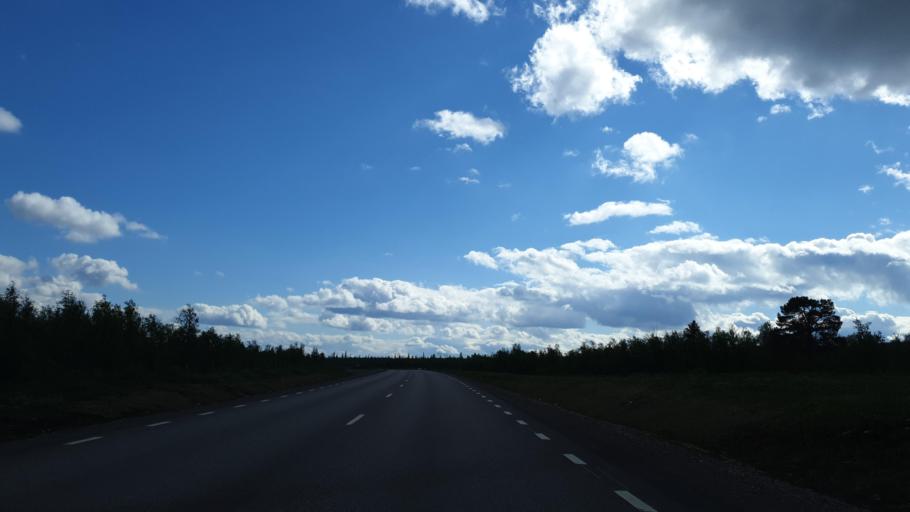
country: SE
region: Norrbotten
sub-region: Kiruna Kommun
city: Kiruna
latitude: 67.8133
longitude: 20.2391
